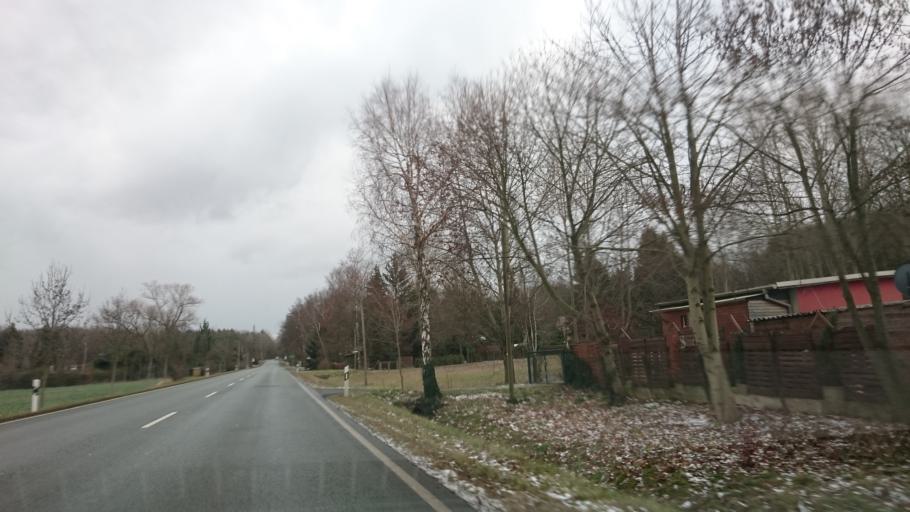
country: DE
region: Saxony
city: Hartmannsdorf
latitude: 50.7313
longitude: 12.4154
